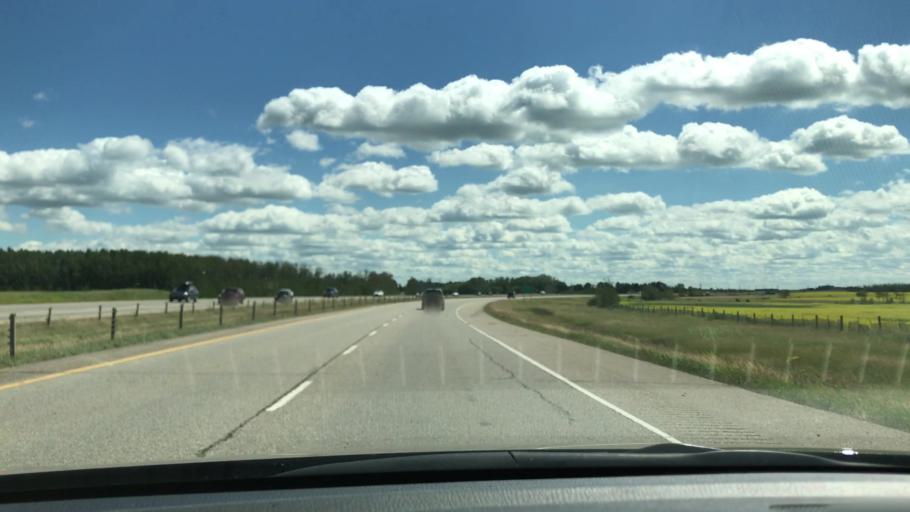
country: CA
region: Alberta
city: Leduc
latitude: 53.2456
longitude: -113.5621
